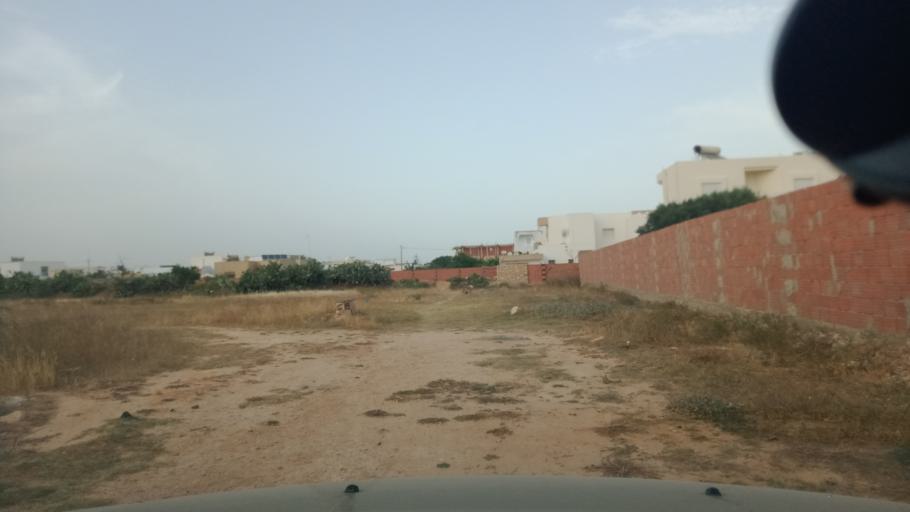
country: TN
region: Safaqis
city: Al Qarmadah
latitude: 34.7923
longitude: 10.7709
